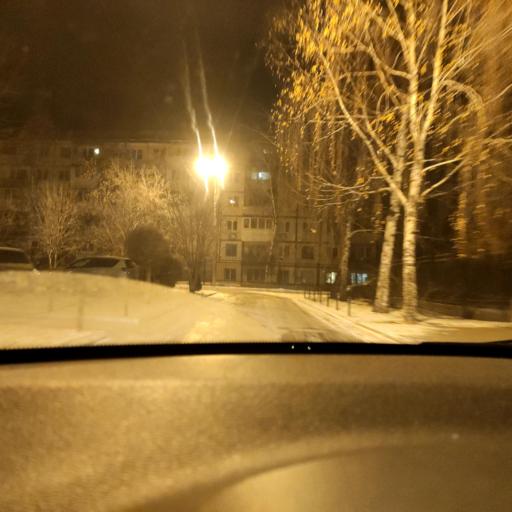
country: RU
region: Samara
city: Samara
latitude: 53.2363
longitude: 50.2274
